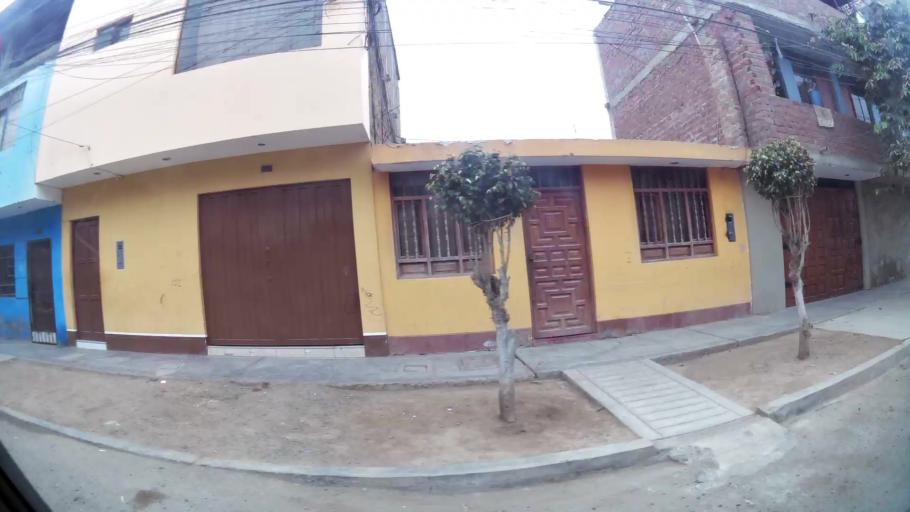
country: PE
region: La Libertad
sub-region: Provincia de Trujillo
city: Buenos Aires
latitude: -8.1391
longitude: -79.0469
